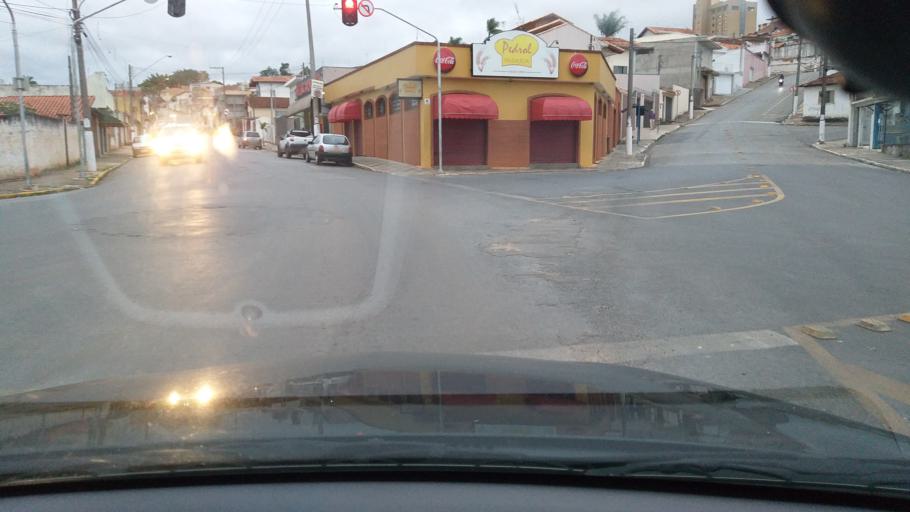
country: BR
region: Sao Paulo
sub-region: Itapeva
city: Itapeva
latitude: -23.9805
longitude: -48.8726
